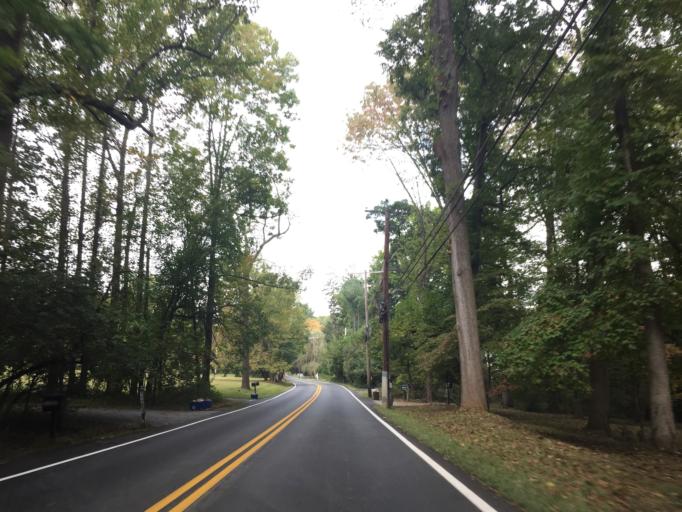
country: US
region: Maryland
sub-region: Baltimore County
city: Mays Chapel
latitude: 39.4328
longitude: -76.7003
